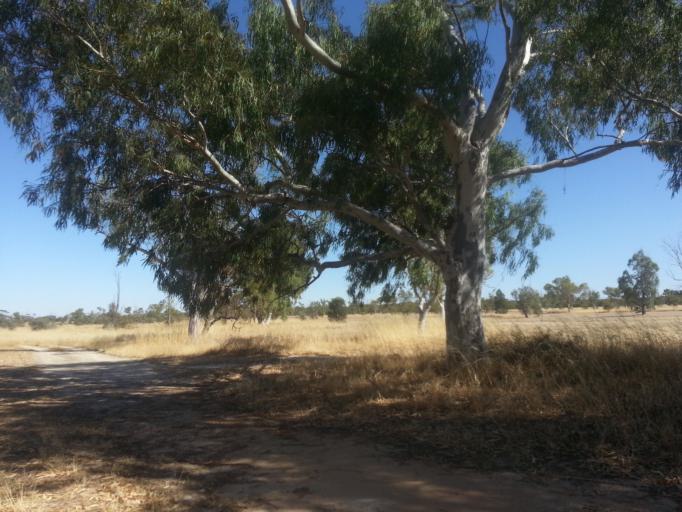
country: AU
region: Western Australia
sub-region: Wongan-Ballidu
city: Wongan Hills
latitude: -30.6054
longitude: 116.7696
